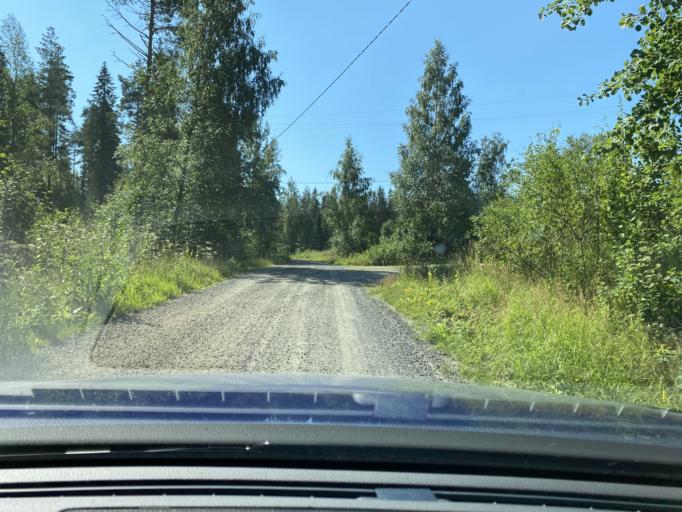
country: FI
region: Central Finland
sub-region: Jaemsae
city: Jaemsae
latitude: 61.8588
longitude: 25.3939
